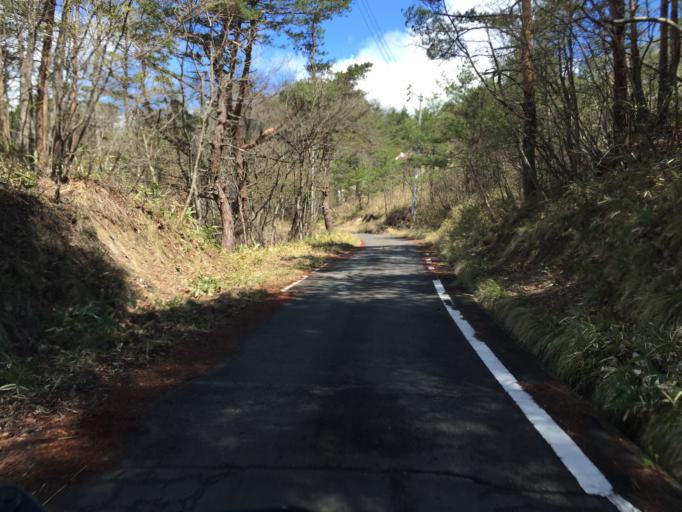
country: JP
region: Fukushima
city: Fukushima-shi
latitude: 37.8466
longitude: 140.4312
